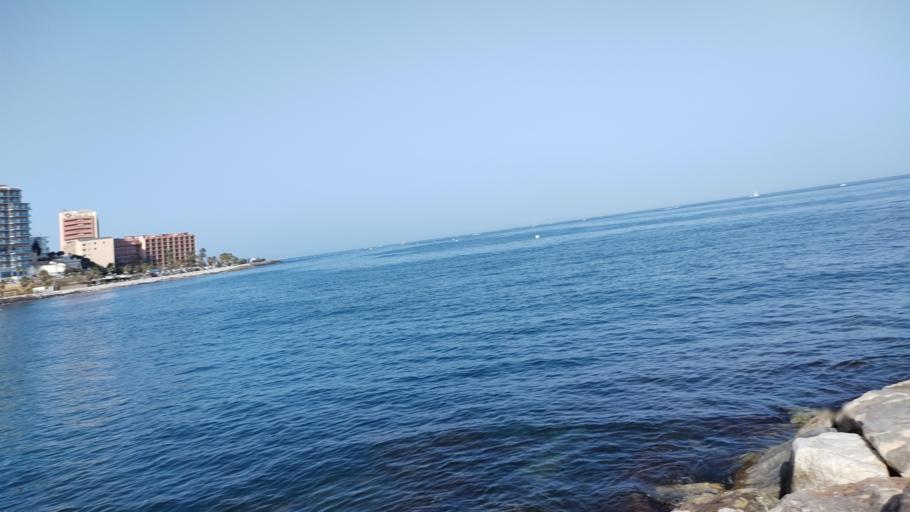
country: ES
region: Andalusia
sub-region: Provincia de Malaga
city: Benalmadena
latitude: 36.5790
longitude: -4.5394
